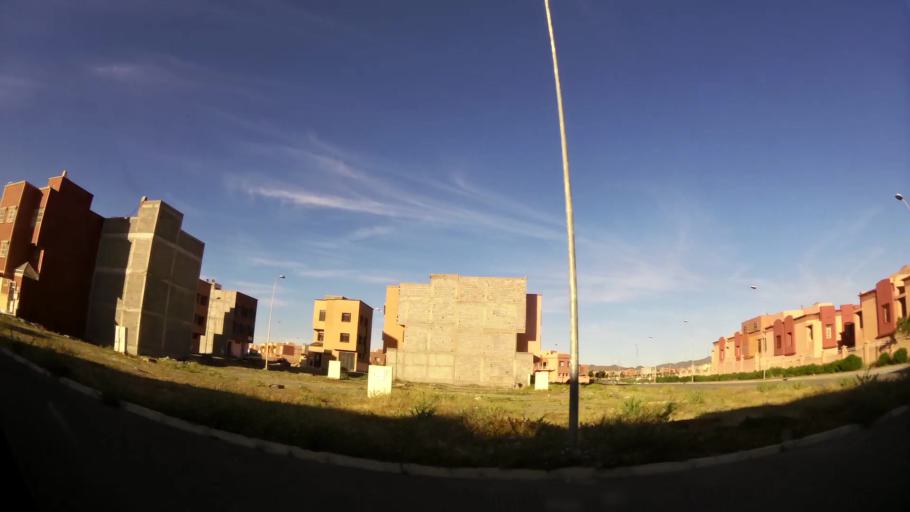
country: MA
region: Marrakech-Tensift-Al Haouz
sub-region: Marrakech
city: Marrakesh
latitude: 31.7589
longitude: -8.1117
